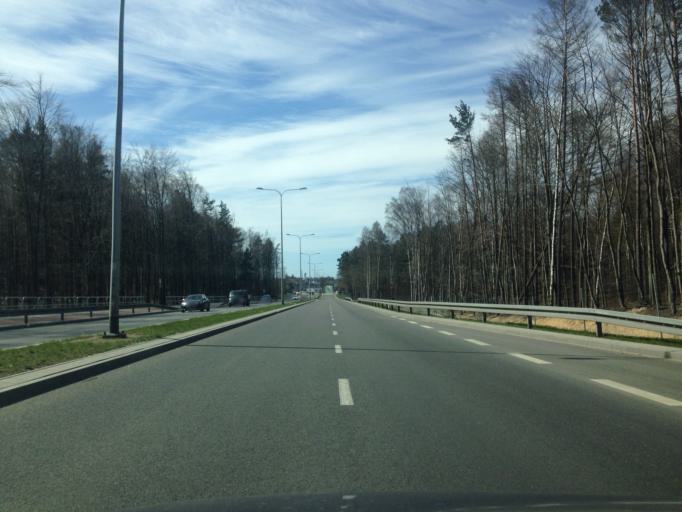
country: PL
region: Pomeranian Voivodeship
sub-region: Gdynia
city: Wielki Kack
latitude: 54.4994
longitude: 18.4795
